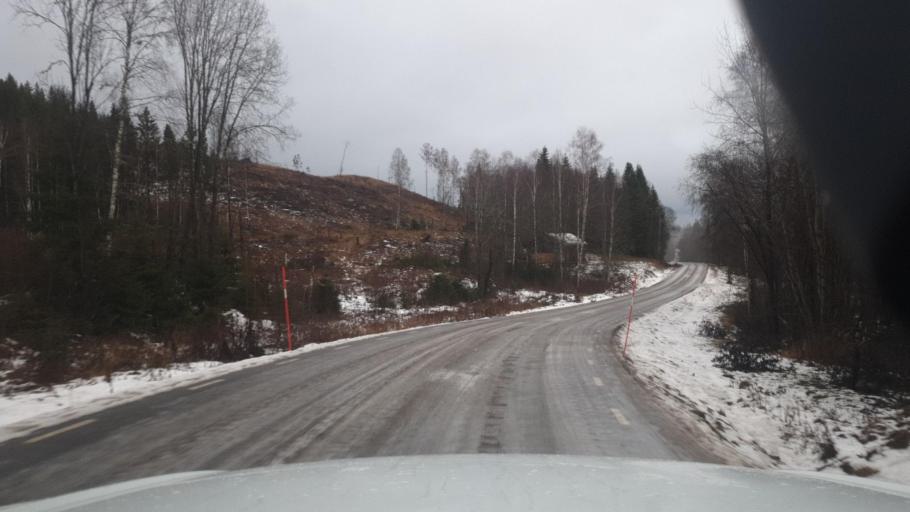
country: SE
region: Vaermland
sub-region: Torsby Kommun
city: Torsby
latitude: 59.9794
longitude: 12.8143
